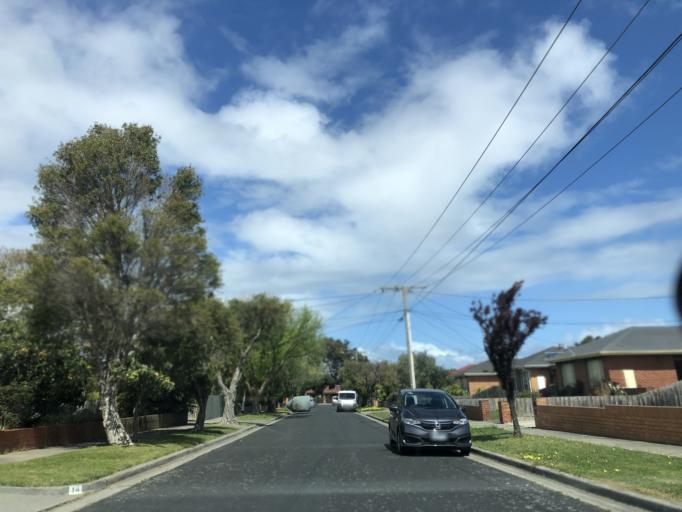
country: AU
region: Victoria
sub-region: Monash
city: Oakleigh South
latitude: -37.9375
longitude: 145.0878
